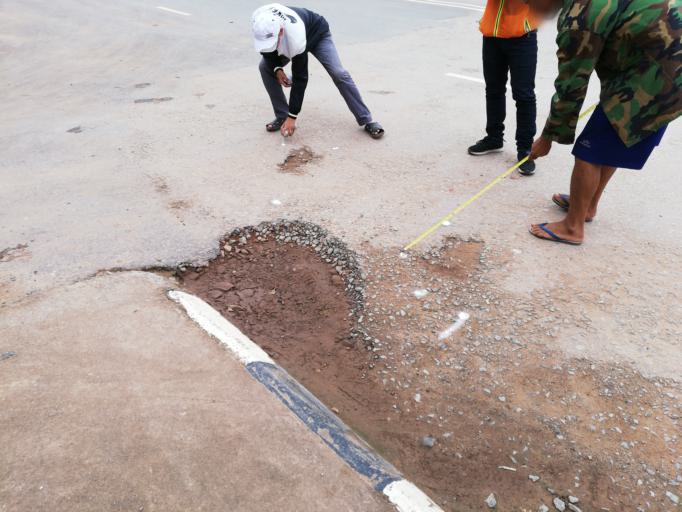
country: LA
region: Loungnamtha
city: Louang Namtha
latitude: 21.0036
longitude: 101.4074
